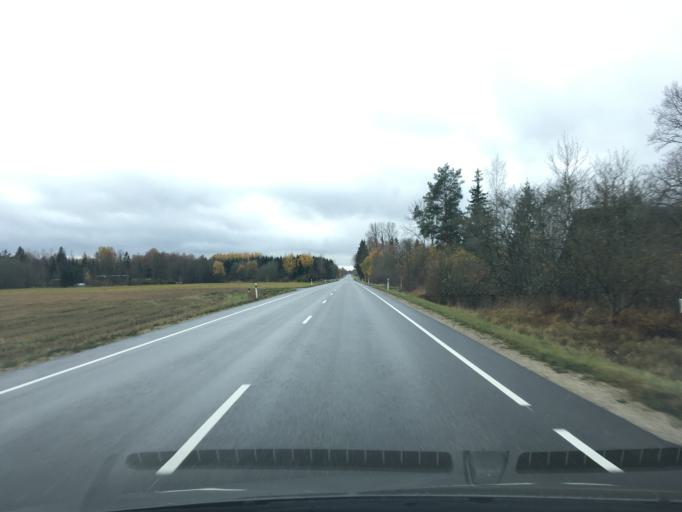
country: EE
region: Jogevamaa
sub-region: Tabivere vald
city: Tabivere
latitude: 58.4443
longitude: 26.5095
